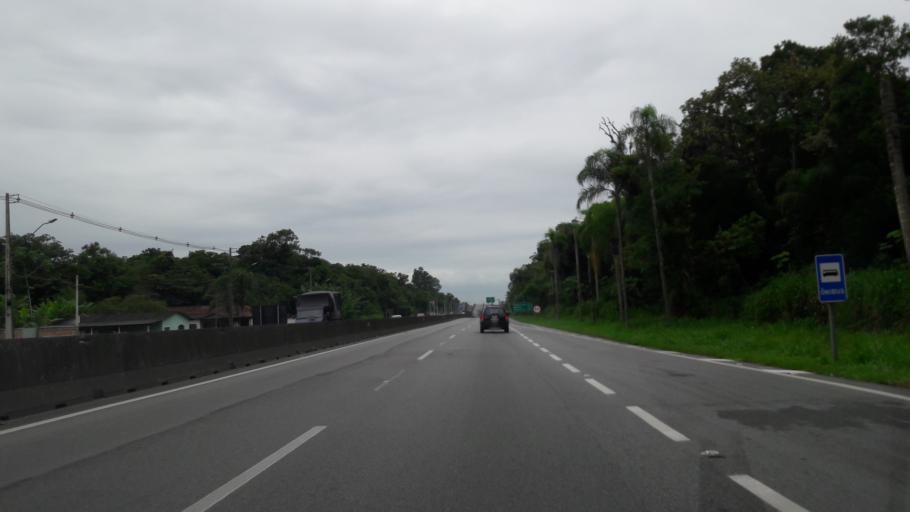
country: BR
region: Parana
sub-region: Paranagua
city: Paranagua
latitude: -25.5637
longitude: -48.5800
